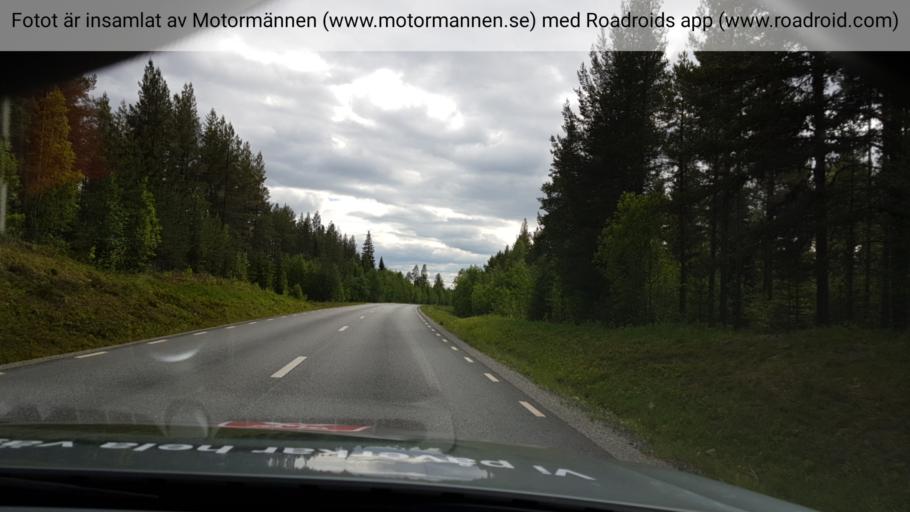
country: SE
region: Jaemtland
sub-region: Stroemsunds Kommun
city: Stroemsund
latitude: 63.9910
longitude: 15.5084
